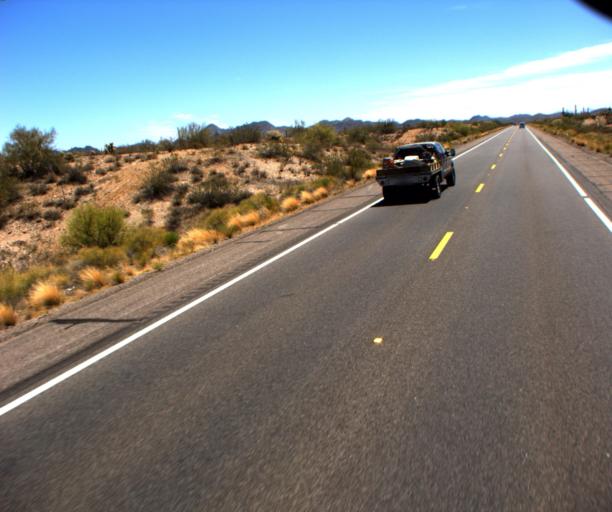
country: US
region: Arizona
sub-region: Maricopa County
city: Sun City West
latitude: 33.8337
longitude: -112.4558
